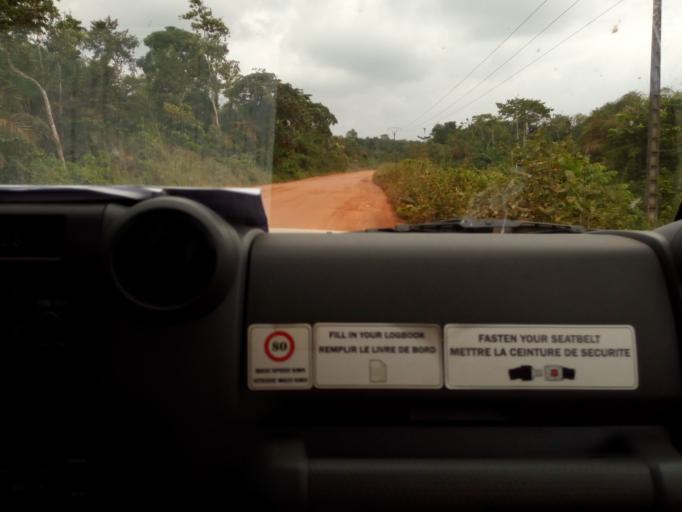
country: CI
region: Bas-Sassandra
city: Tabou
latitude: 4.5258
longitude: -7.2590
